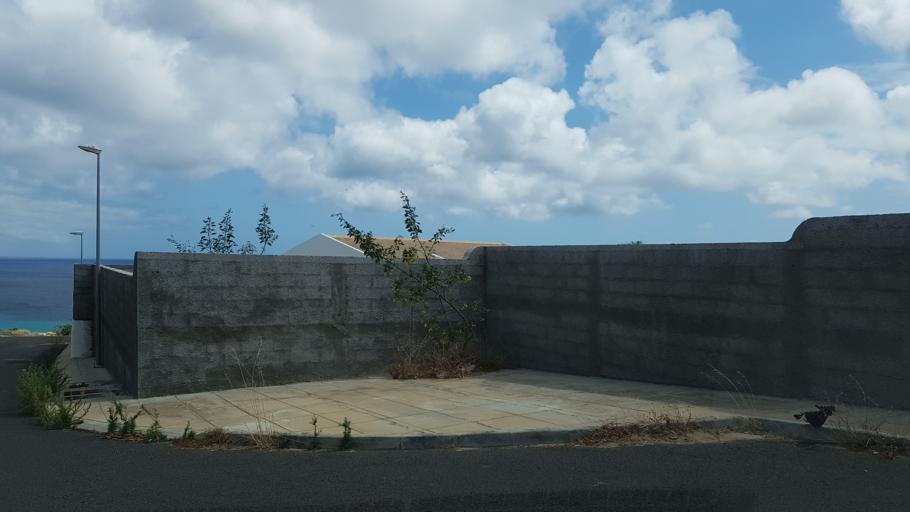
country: PT
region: Madeira
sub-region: Porto Santo
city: Vila de Porto Santo
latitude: 33.0555
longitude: -16.3448
